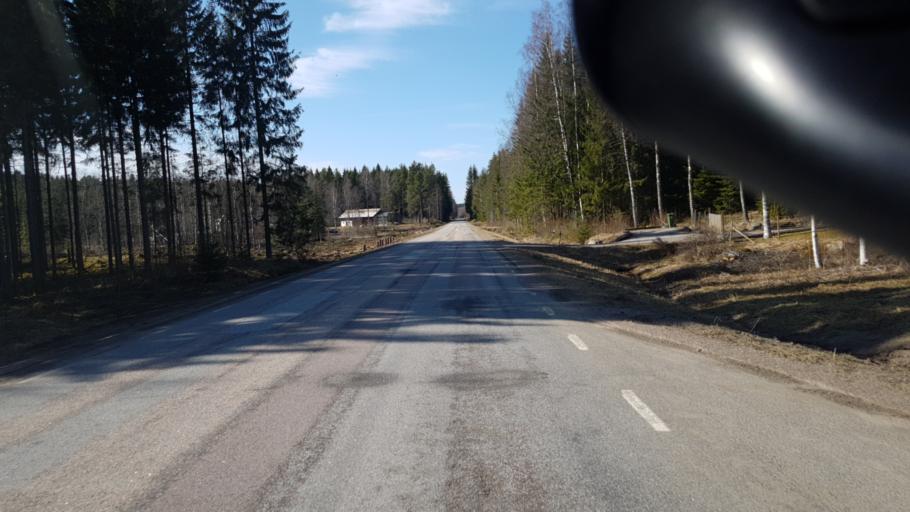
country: SE
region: Vaermland
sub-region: Arvika Kommun
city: Arvika
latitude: 59.6520
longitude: 12.7352
